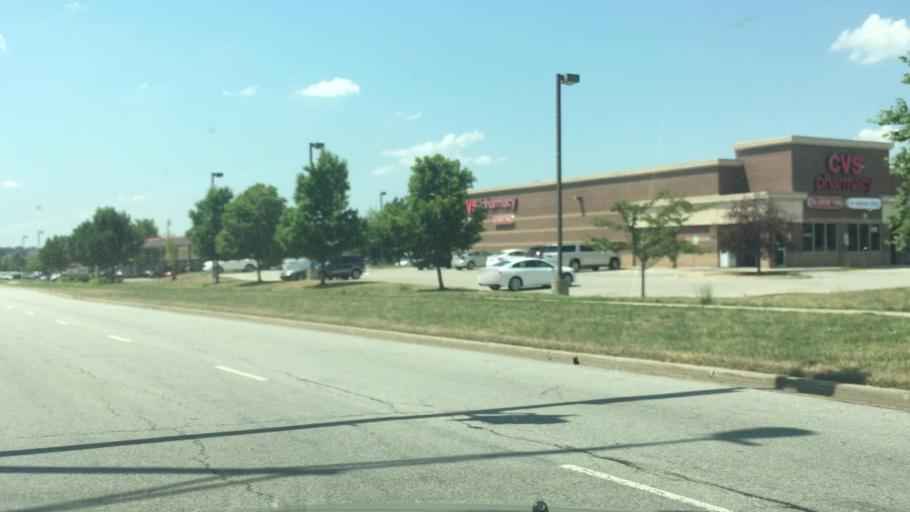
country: US
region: Kansas
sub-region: Johnson County
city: Lenexa
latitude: 38.8871
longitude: -94.7238
